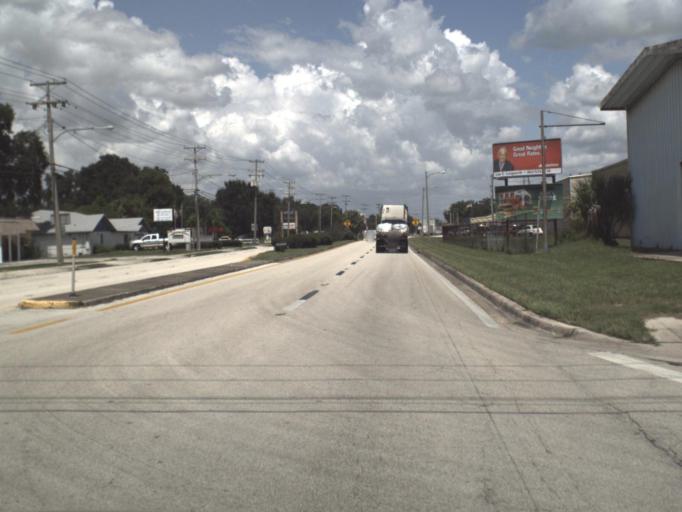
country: US
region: Florida
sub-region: Polk County
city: Bartow
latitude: 27.8788
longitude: -81.8286
